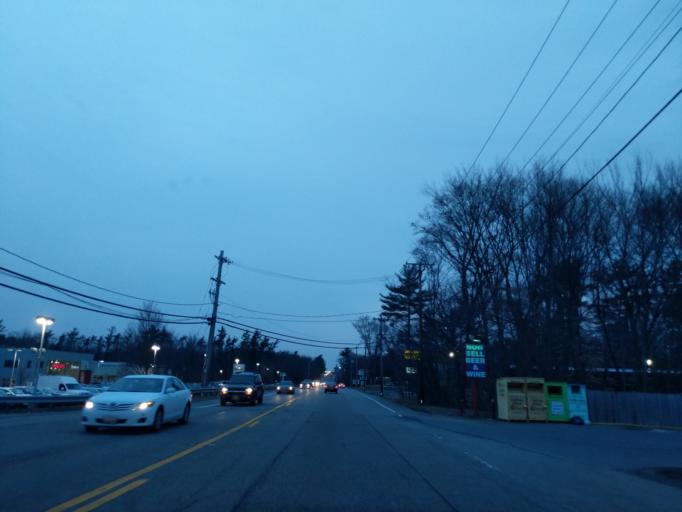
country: US
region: Massachusetts
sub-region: Bristol County
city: Raynham Center
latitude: 41.9044
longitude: -71.0154
